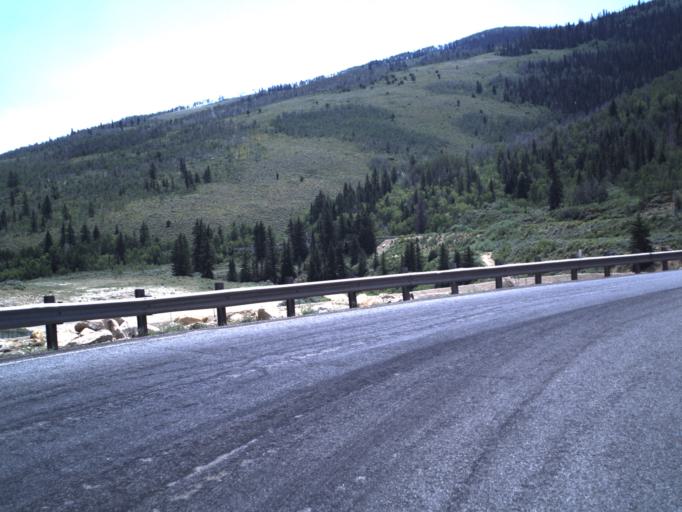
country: US
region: Utah
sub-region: Carbon County
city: Helper
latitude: 39.7875
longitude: -111.1198
